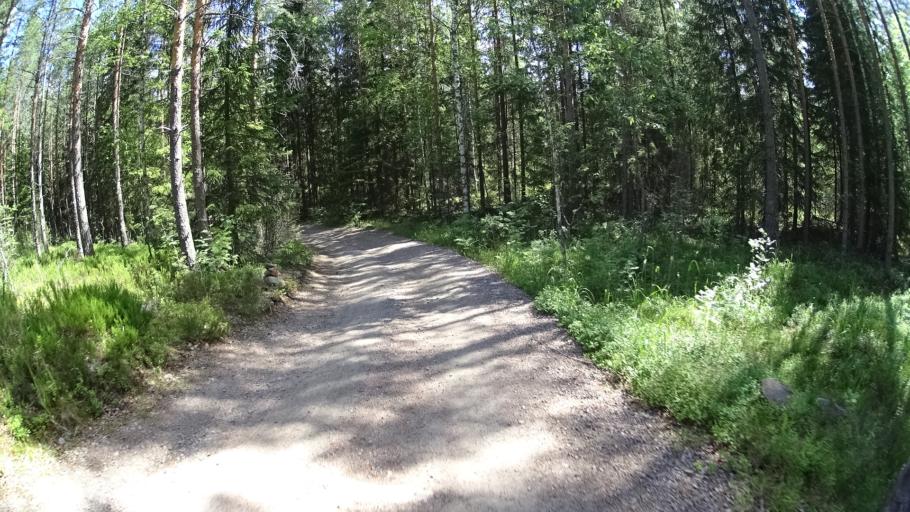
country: FI
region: Uusimaa
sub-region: Helsinki
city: Vihti
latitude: 60.3252
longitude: 24.4826
